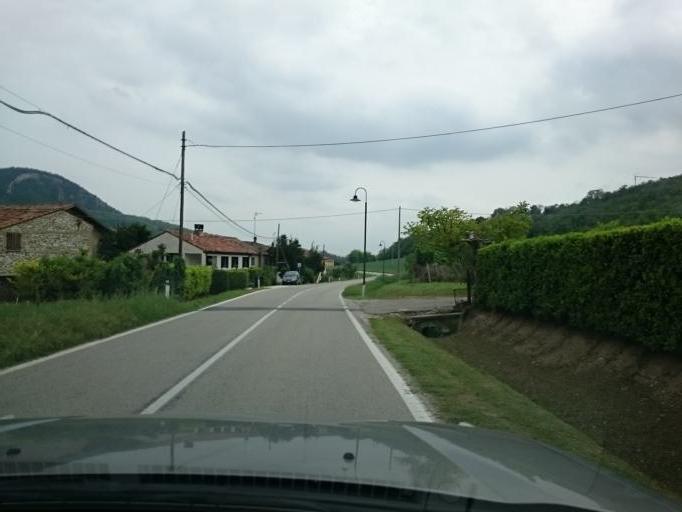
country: IT
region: Veneto
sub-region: Provincia di Padova
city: Arqua Petrarca
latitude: 45.2656
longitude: 11.7199
